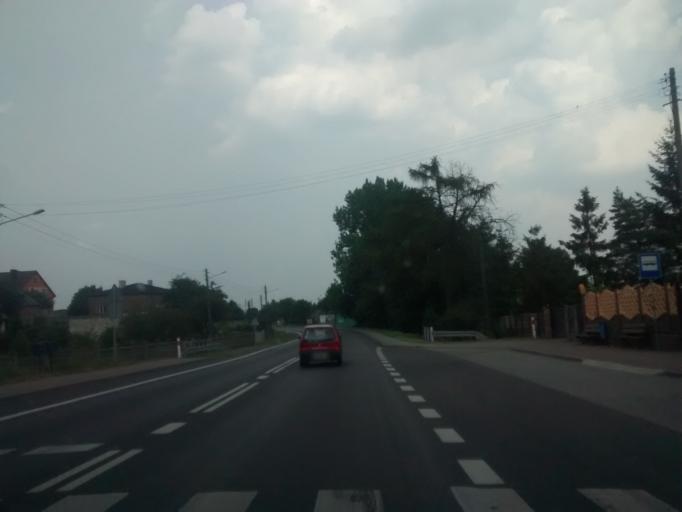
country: PL
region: Silesian Voivodeship
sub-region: Powiat zawiercianski
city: Kroczyce
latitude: 50.5127
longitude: 19.5392
